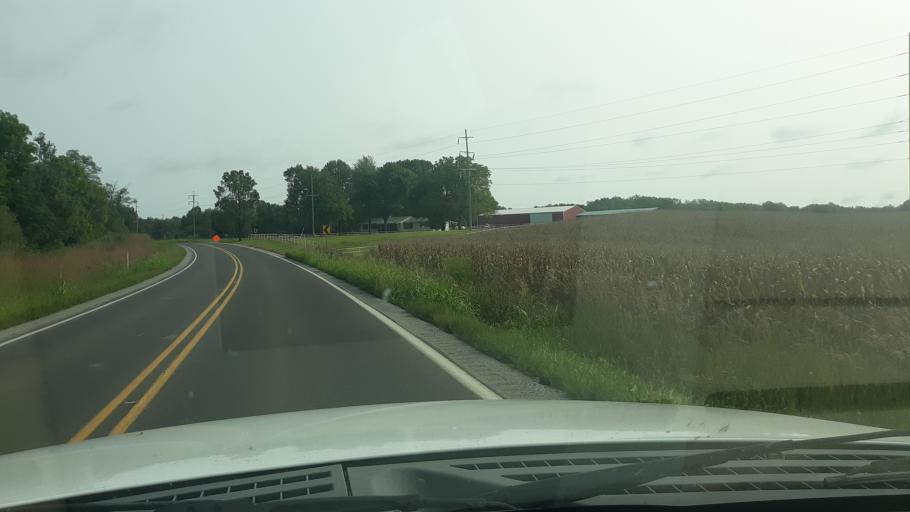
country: US
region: Illinois
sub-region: White County
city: Norris City
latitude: 37.9027
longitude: -88.3606
